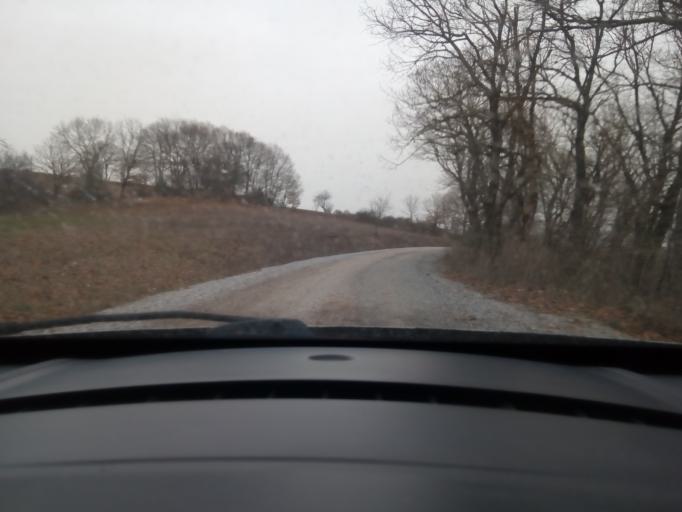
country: TR
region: Balikesir
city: Omerkoy
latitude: 39.8895
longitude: 28.0350
